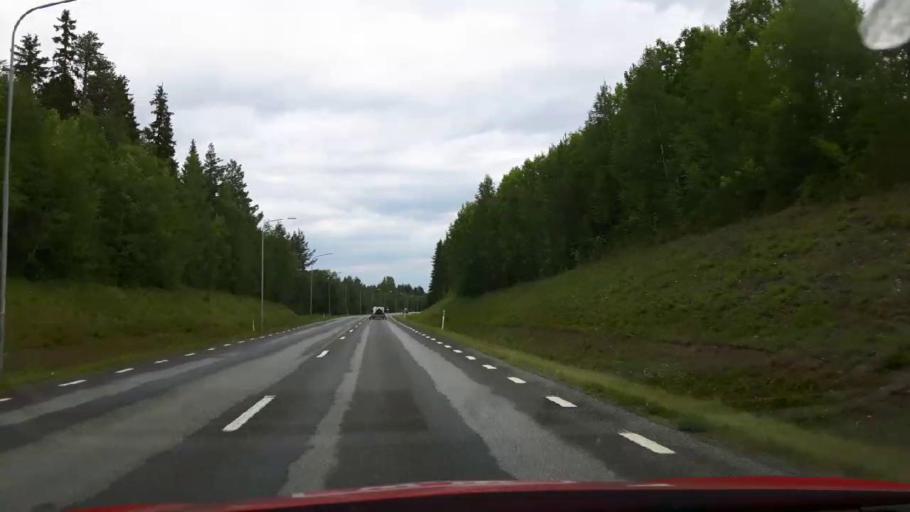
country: SE
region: Jaemtland
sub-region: Stroemsunds Kommun
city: Stroemsund
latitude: 63.6685
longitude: 15.3914
